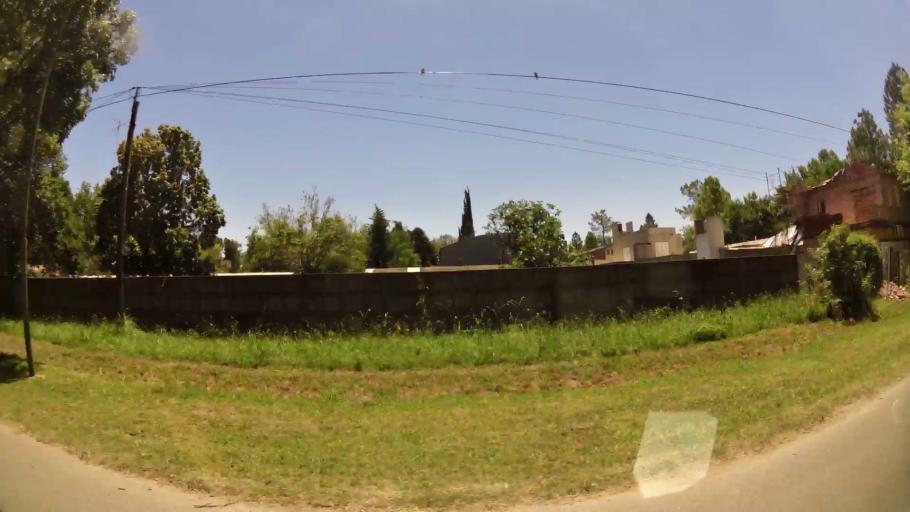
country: AR
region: Santa Fe
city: Rafaela
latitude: -31.2581
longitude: -61.4549
